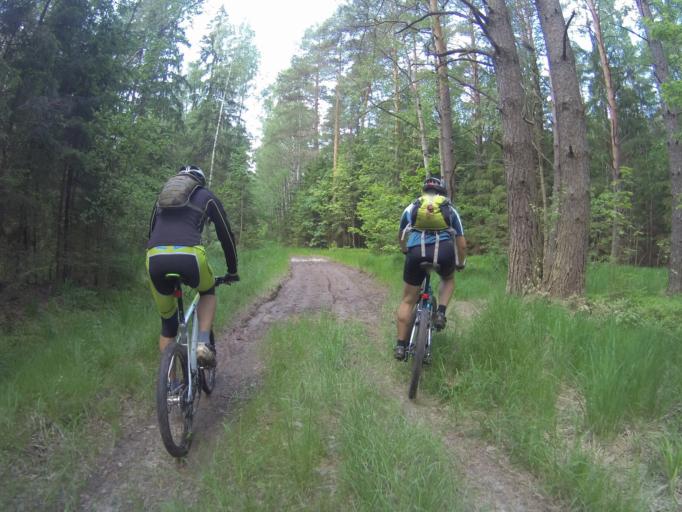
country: RU
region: Vladimir
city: Raduzhnyy
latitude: 56.0248
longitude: 40.2616
